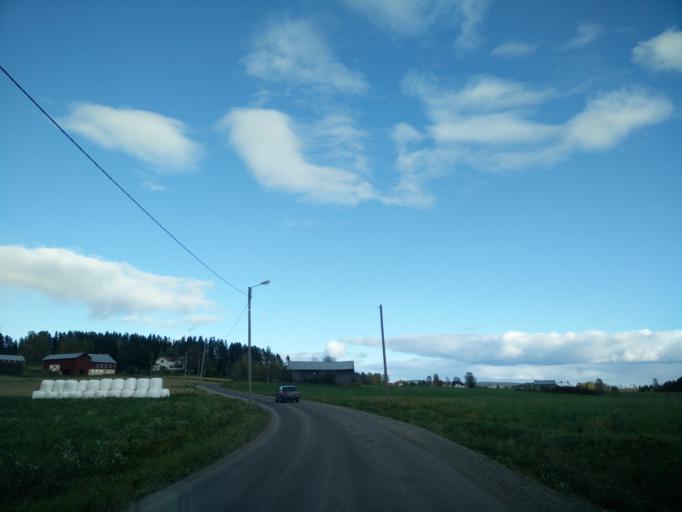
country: SE
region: Vaesternorrland
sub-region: Sundsvalls Kommun
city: Matfors
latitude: 62.3368
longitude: 16.9765
